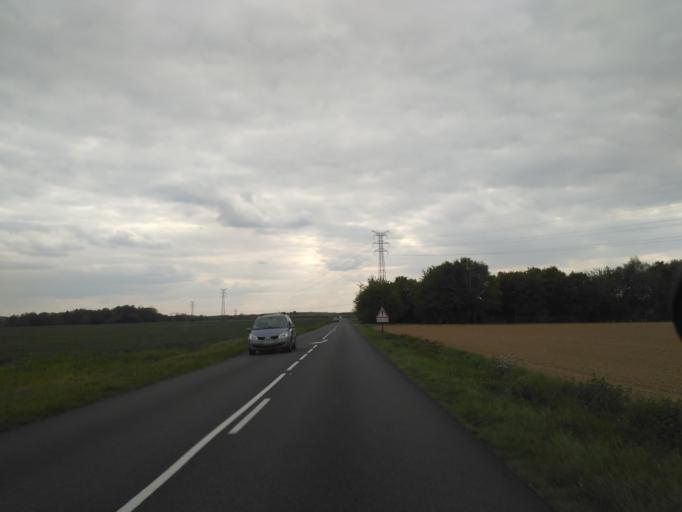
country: FR
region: Ile-de-France
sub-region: Departement de Seine-et-Marne
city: Moisenay
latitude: 48.5756
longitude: 2.7774
